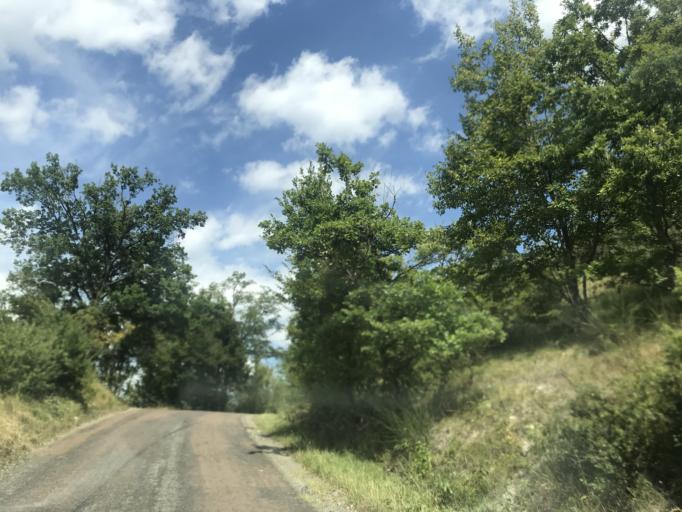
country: IT
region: Emilia-Romagna
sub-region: Provincia di Bologna
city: Vergato
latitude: 44.2438
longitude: 11.1124
